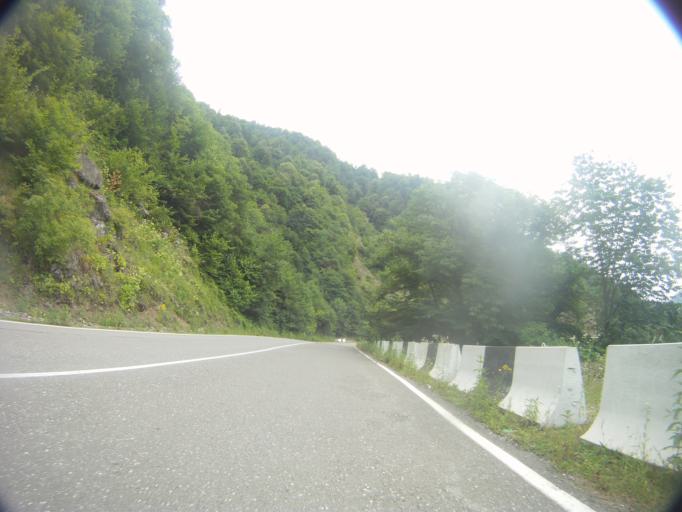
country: GE
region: Samegrelo and Zemo Svaneti
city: Jvari
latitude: 42.8085
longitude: 42.0434
